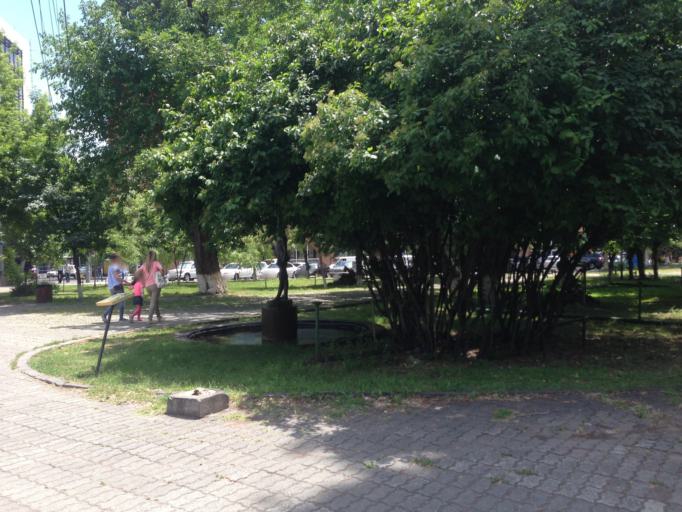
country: AM
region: Yerevan
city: Yerevan
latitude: 40.1760
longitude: 44.5085
